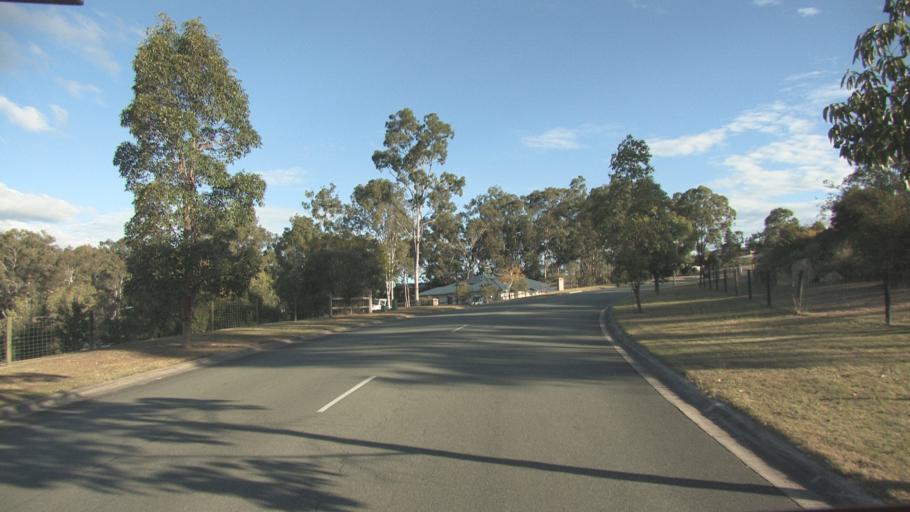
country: AU
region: Queensland
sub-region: Logan
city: Cedar Vale
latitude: -27.8728
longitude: 153.0761
